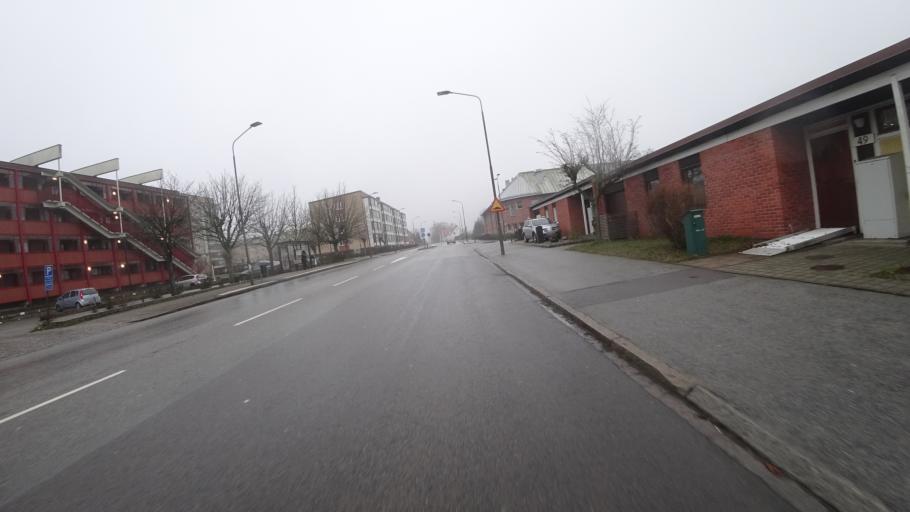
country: SE
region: Skane
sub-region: Malmo
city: Malmoe
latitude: 55.5733
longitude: 13.0141
